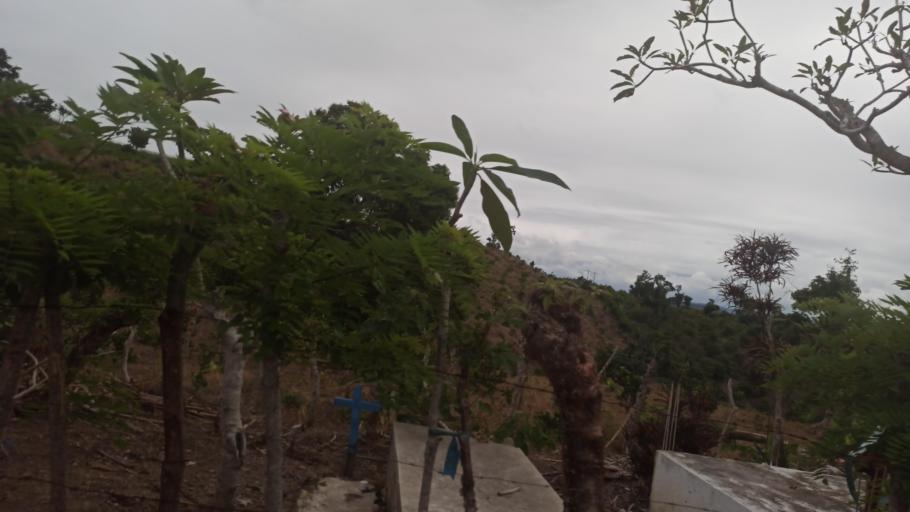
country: MX
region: Veracruz
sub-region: Papantla
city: Residencial Tajin
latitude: 20.6092
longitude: -97.3534
